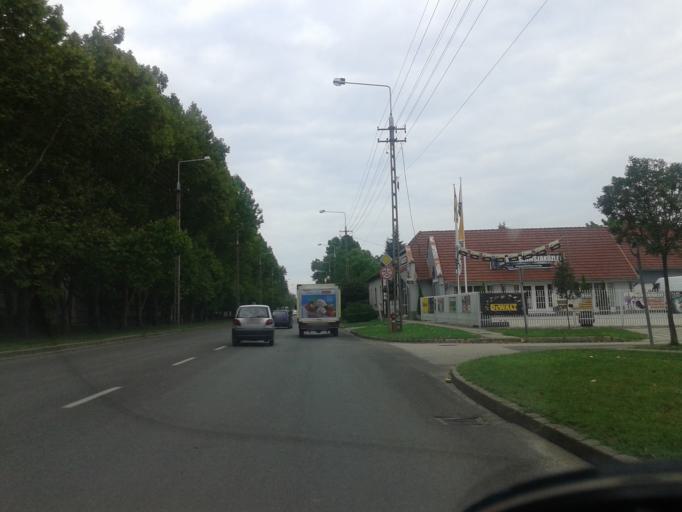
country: HU
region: Bacs-Kiskun
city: Kiskunhalas
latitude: 46.4362
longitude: 19.4846
